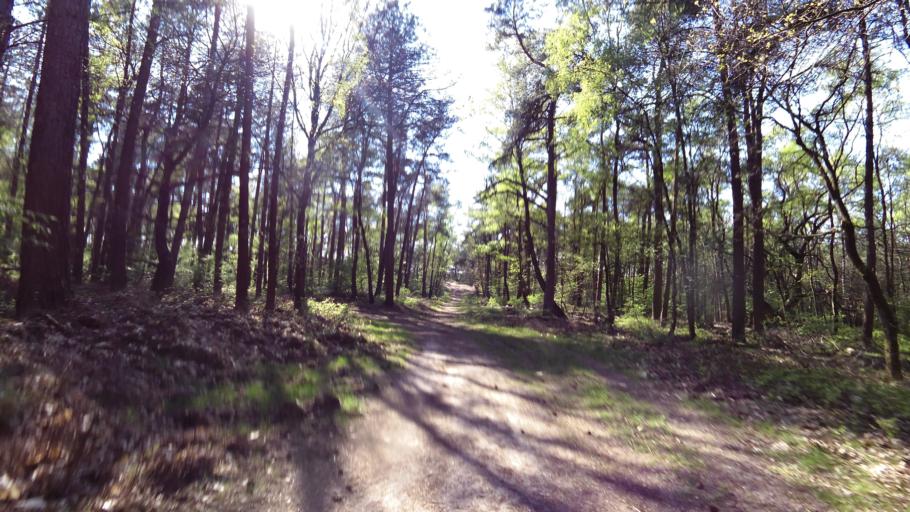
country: NL
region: Gelderland
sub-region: Gemeente Rozendaal
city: Rozendaal
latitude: 52.0175
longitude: 5.9425
